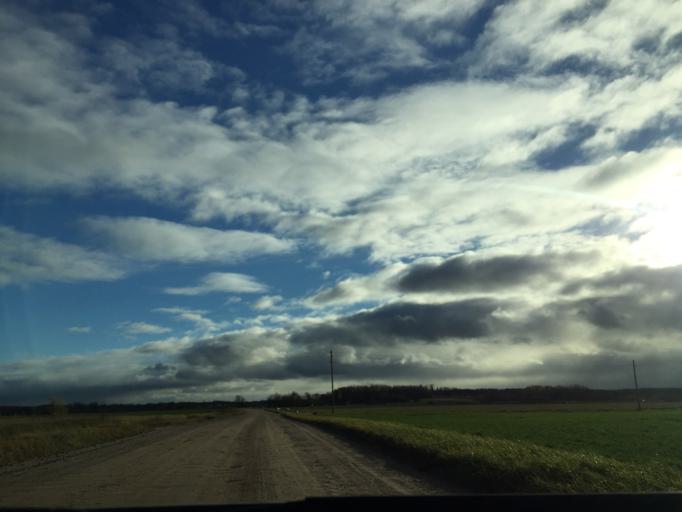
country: LV
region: Kandava
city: Kandava
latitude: 56.9560
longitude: 22.9456
